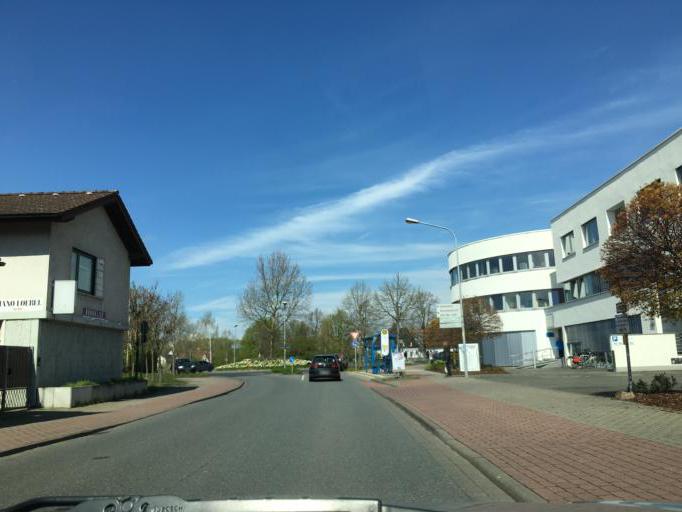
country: DE
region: Hesse
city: Dieburg
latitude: 49.8933
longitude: 8.8325
